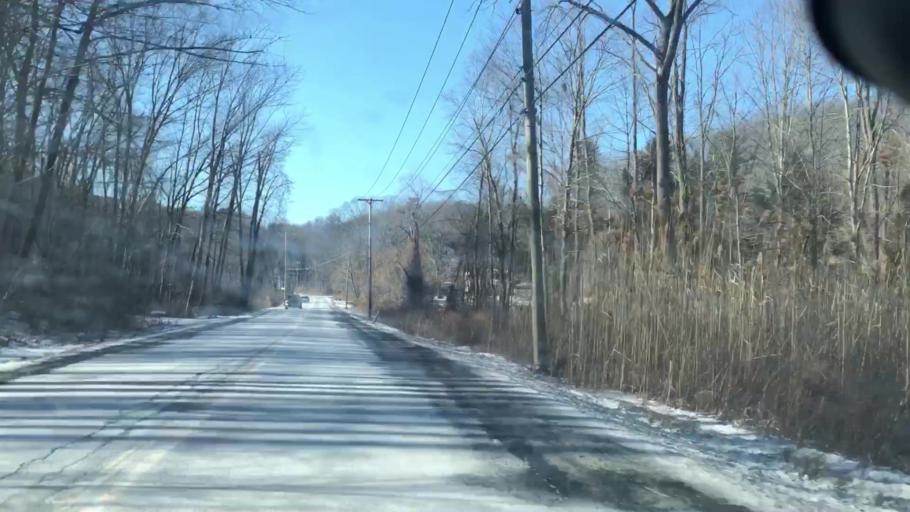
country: US
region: New York
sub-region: Putnam County
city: Carmel Hamlet
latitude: 41.3882
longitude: -73.6894
